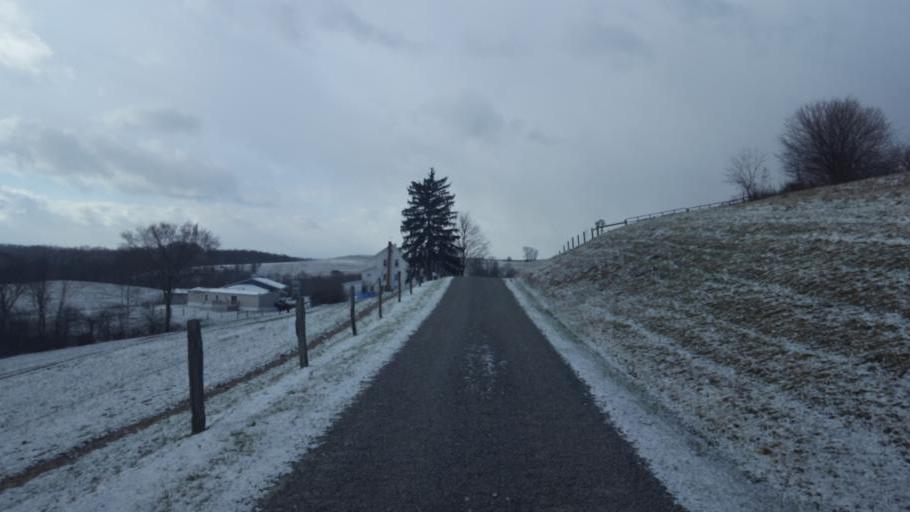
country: US
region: Ohio
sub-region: Holmes County
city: Millersburg
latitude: 40.5166
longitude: -81.8132
